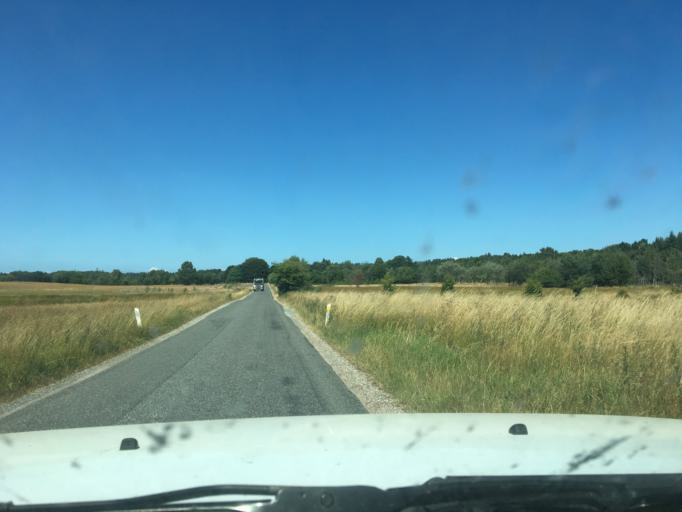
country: DK
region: Central Jutland
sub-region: Syddjurs Kommune
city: Ryomgard
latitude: 56.4780
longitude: 10.5938
